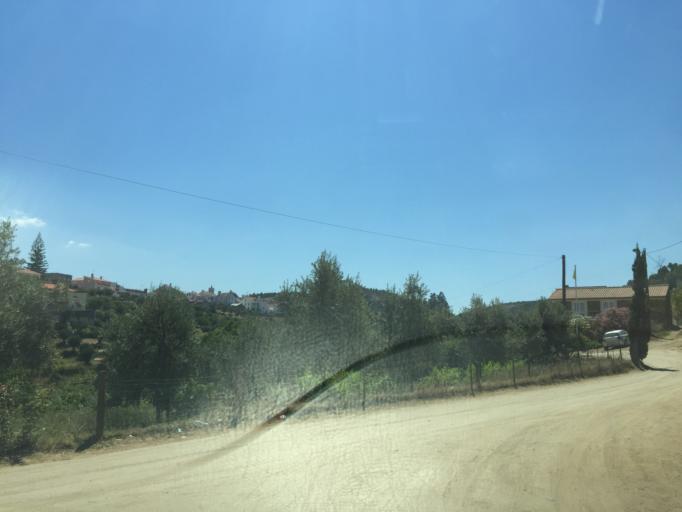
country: PT
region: Santarem
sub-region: Constancia
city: Constancia
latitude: 39.5445
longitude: -8.2770
